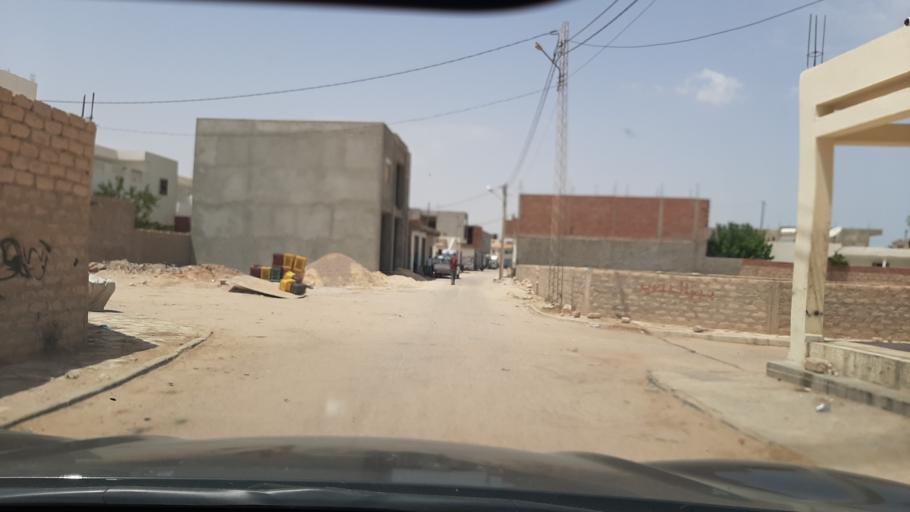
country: TN
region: Qabis
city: Gabes
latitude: 33.6186
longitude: 10.2912
